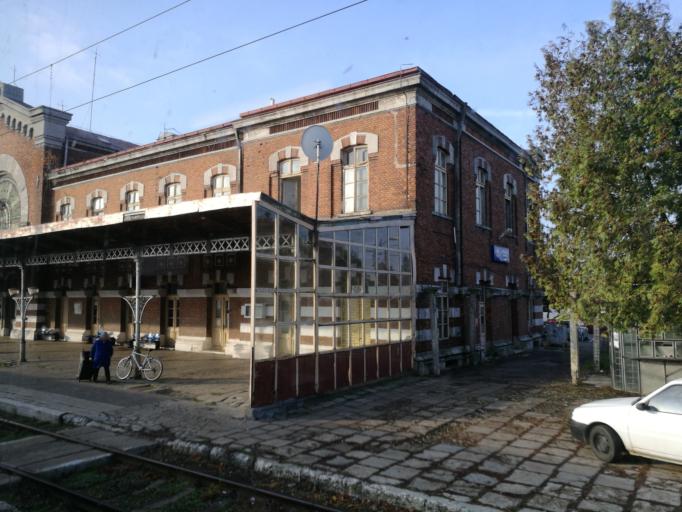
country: RO
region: Buzau
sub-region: Municipiul Ramnicu Sarat
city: Ramnicu Sarat
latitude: 45.3799
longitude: 27.0581
